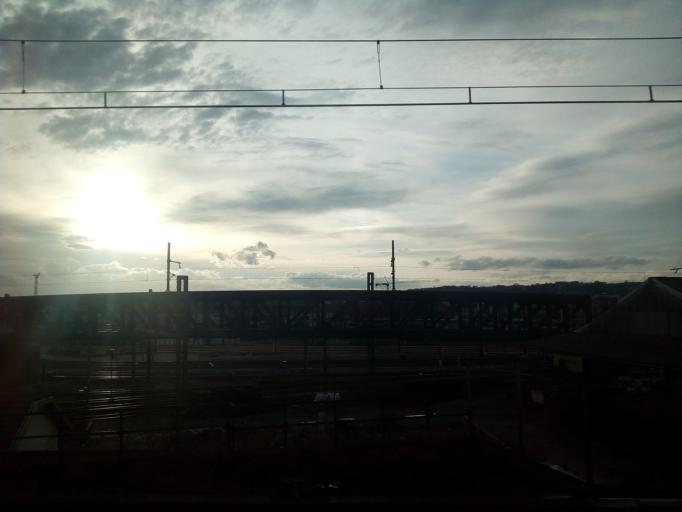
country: FR
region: Rhone-Alpes
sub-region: Departement du Rhone
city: Lyon
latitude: 45.7397
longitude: 4.8488
